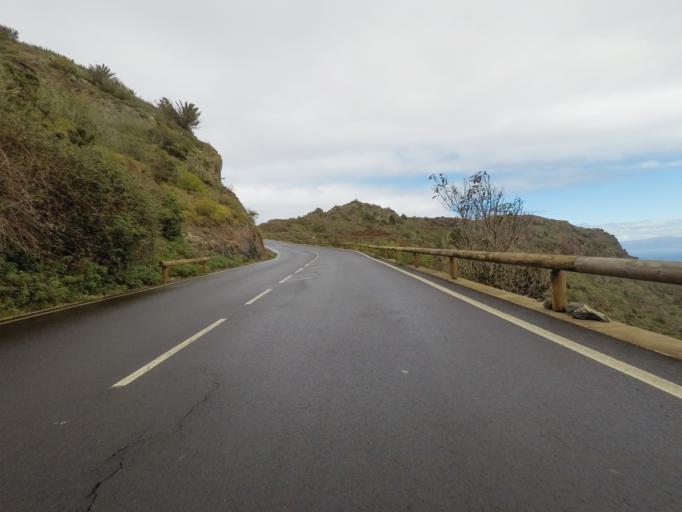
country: ES
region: Canary Islands
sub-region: Provincia de Santa Cruz de Tenerife
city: Agulo
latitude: 28.1882
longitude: -17.2209
